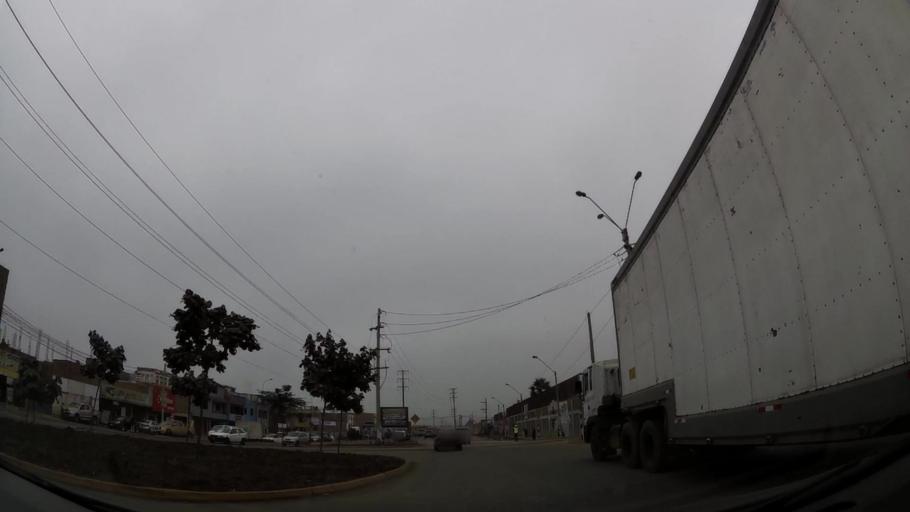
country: PE
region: Lima
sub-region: Lima
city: Punta Hermosa
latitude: -12.2948
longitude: -76.8523
